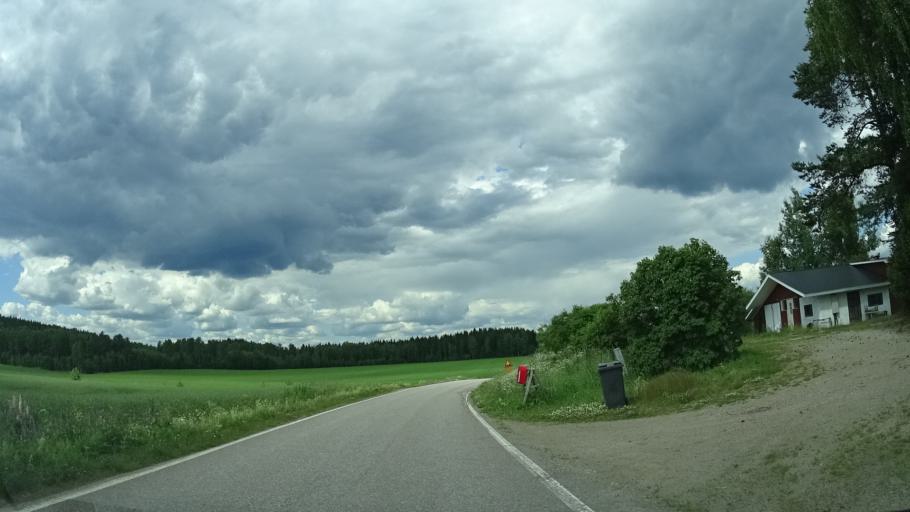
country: FI
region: Uusimaa
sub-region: Helsinki
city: Vihti
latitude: 60.4181
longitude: 24.5424
